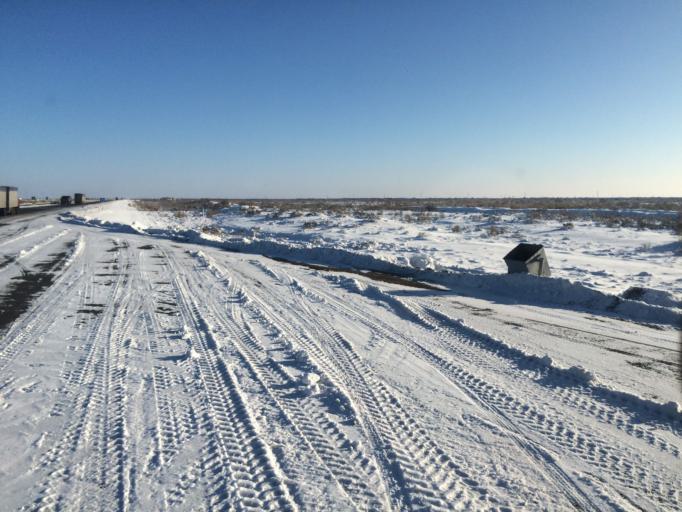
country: KZ
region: Qyzylorda
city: Belkol
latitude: 44.7733
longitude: 65.7637
